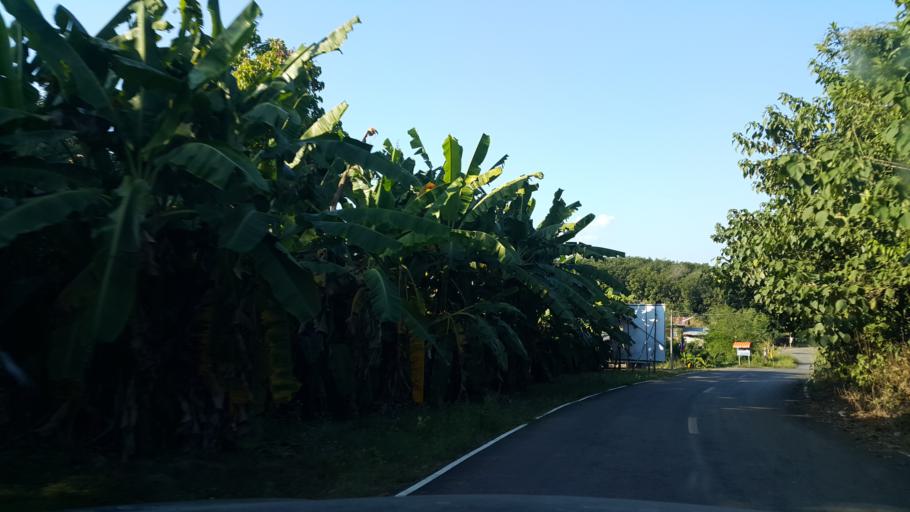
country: TH
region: Sukhothai
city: Thung Saliam
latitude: 17.4051
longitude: 99.5126
